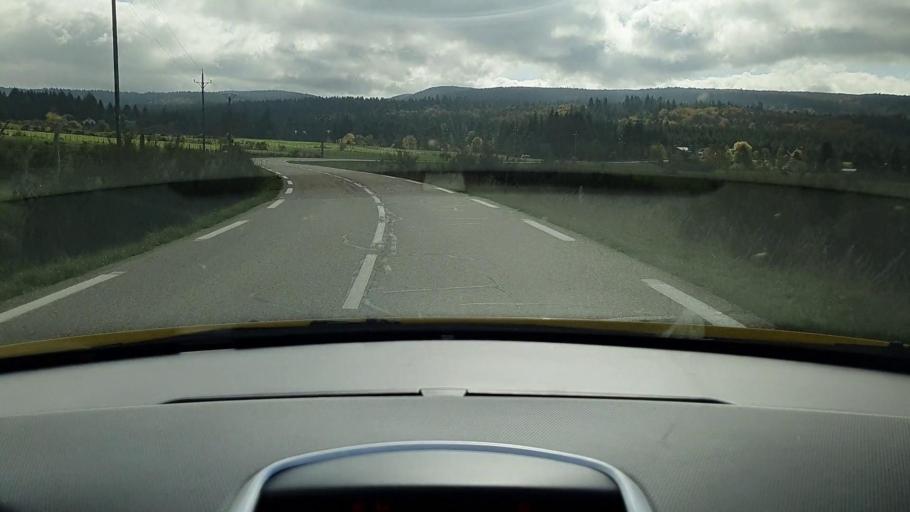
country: FR
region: Languedoc-Roussillon
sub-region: Departement de la Lozere
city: Meyrueis
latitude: 44.1175
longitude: 3.4837
